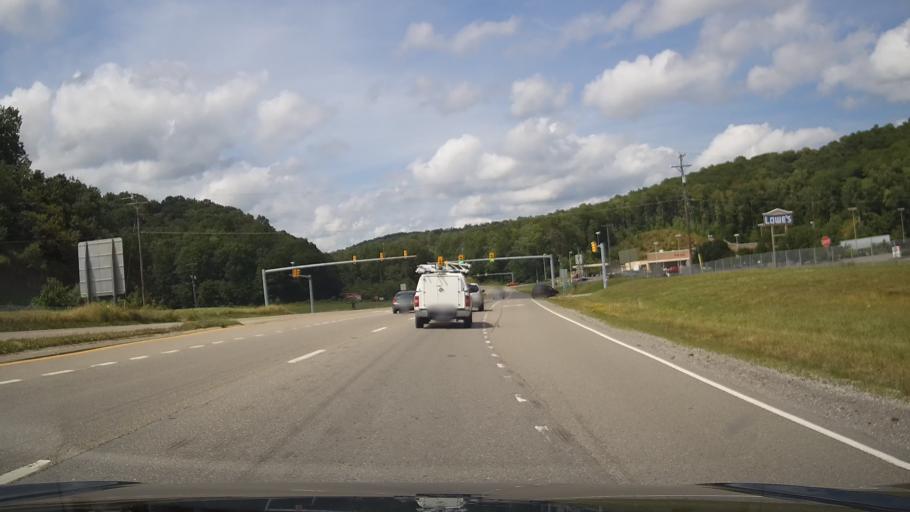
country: US
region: Virginia
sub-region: Wise County
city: Wise
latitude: 36.9731
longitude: -82.5949
